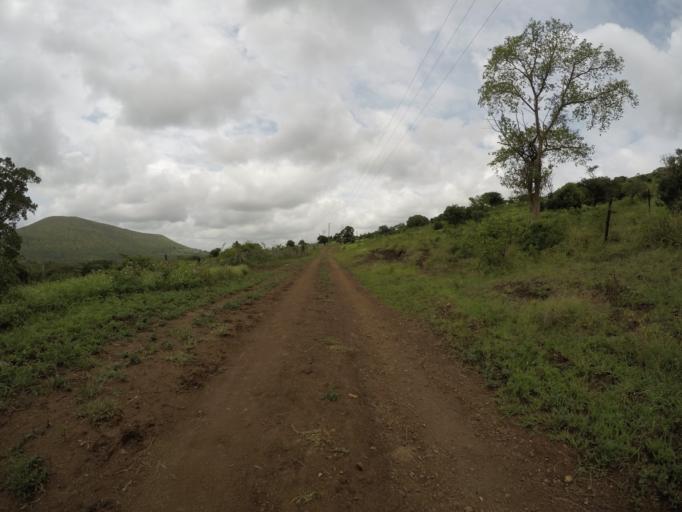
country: ZA
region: KwaZulu-Natal
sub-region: uThungulu District Municipality
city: Empangeni
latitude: -28.5861
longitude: 31.8889
